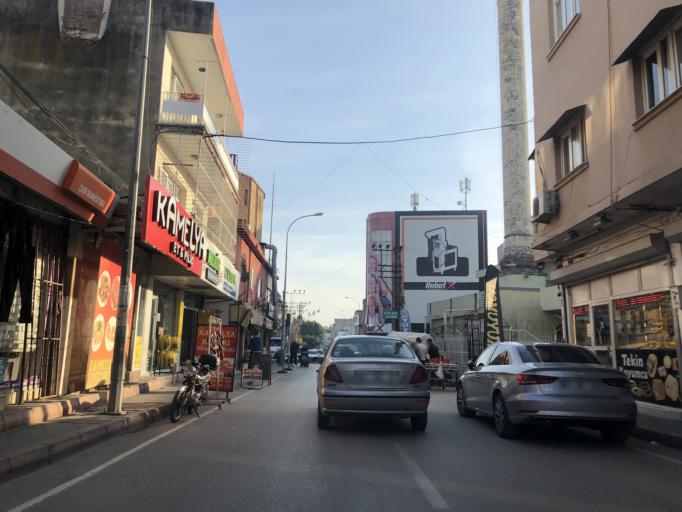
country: TR
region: Adana
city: Adana
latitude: 37.0153
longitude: 35.3145
